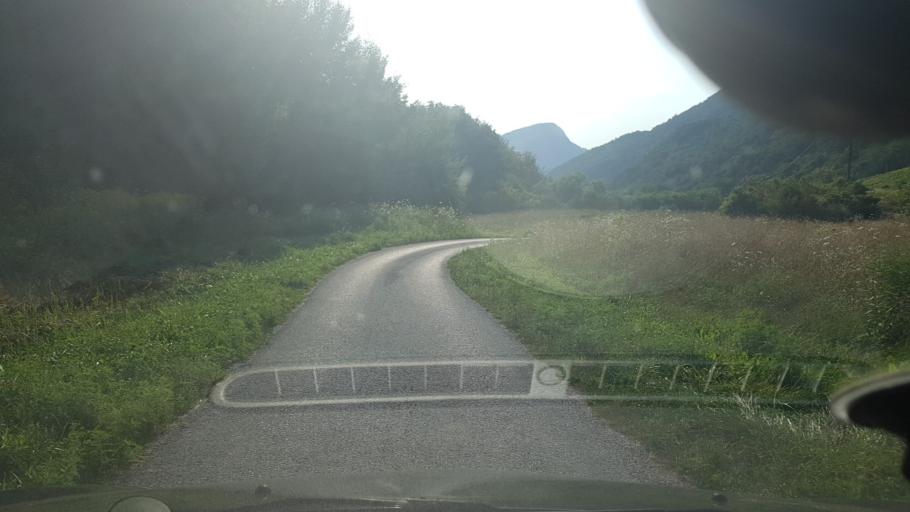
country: HR
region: Krapinsko-Zagorska
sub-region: Grad Krapina
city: Krapina
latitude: 46.1770
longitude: 15.8913
